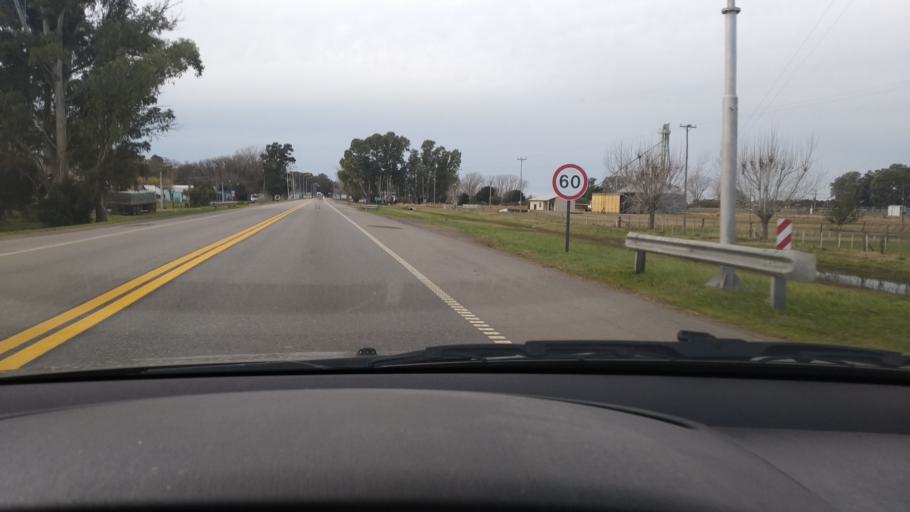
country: AR
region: Buenos Aires
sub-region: Partido de Azul
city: Azul
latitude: -36.3908
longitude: -59.4963
